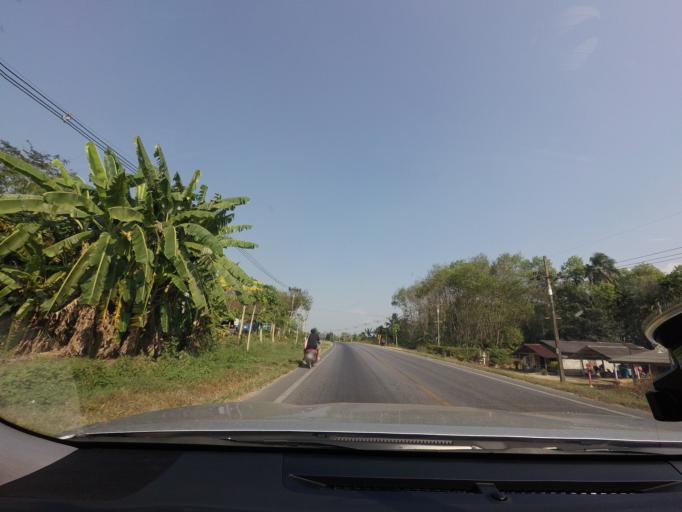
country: TH
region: Surat Thani
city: Phrasaeng
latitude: 8.5603
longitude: 99.1532
